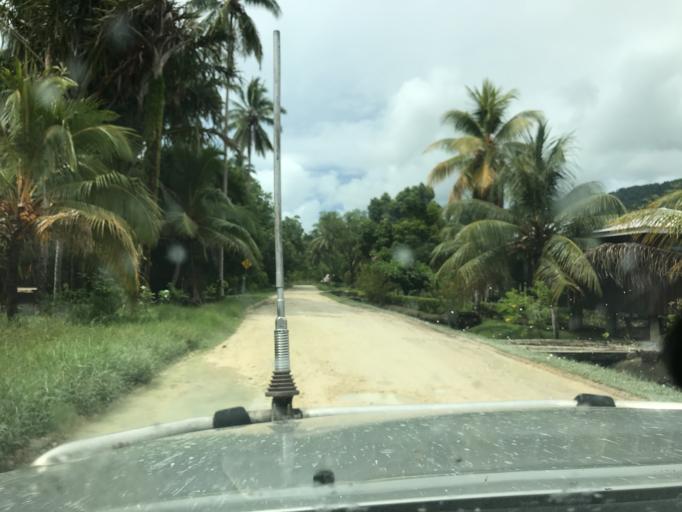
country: SB
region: Malaita
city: Auki
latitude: -8.3428
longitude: 160.6150
